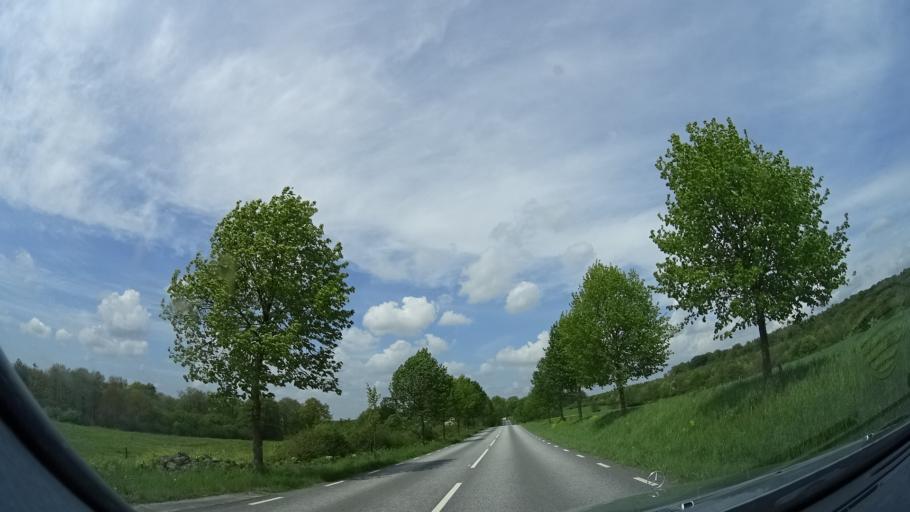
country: SE
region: Skane
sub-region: Sjobo Kommun
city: Sjoebo
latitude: 55.6710
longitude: 13.6646
